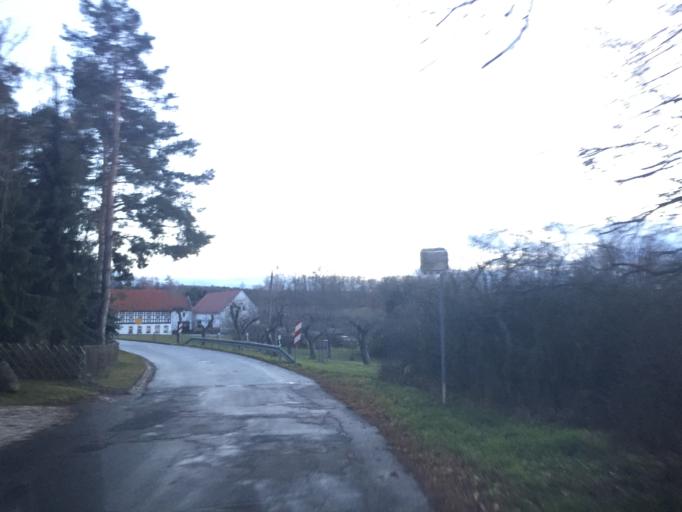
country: DE
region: Thuringia
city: Heyersdorf
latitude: 50.8679
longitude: 12.3309
